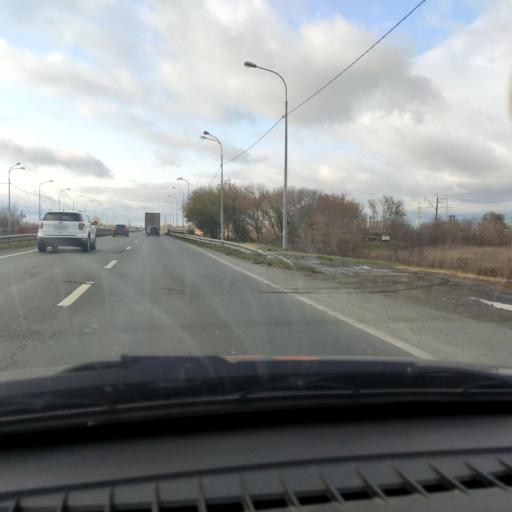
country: RU
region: Samara
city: Tol'yatti
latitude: 53.5738
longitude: 49.4523
